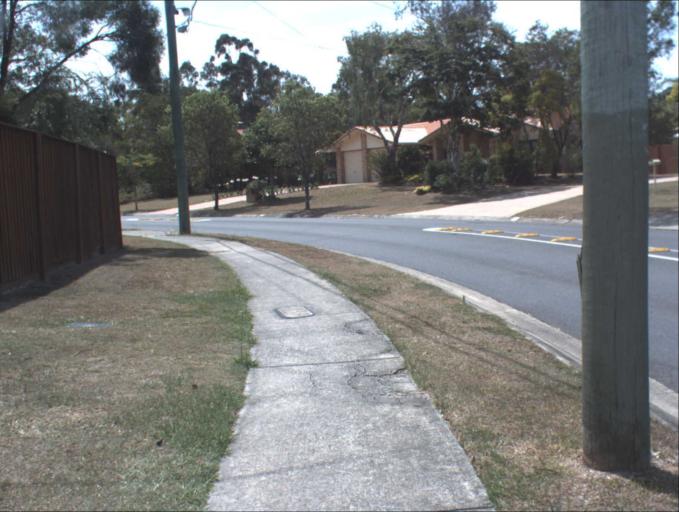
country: AU
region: Queensland
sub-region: Logan
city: Beenleigh
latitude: -27.6625
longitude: 153.2030
